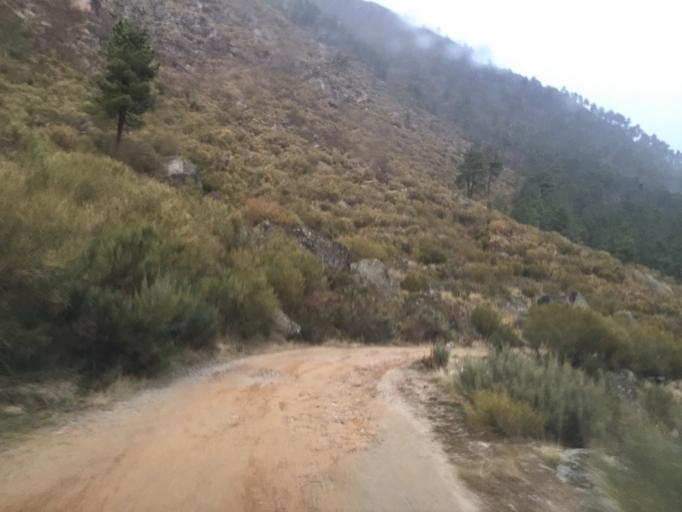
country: PT
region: Guarda
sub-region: Manteigas
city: Manteigas
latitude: 40.3634
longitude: -7.5560
